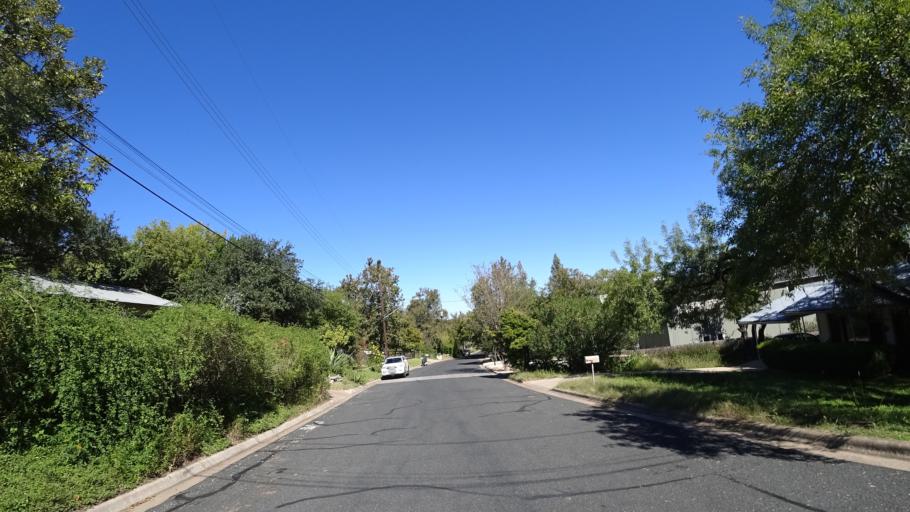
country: US
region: Texas
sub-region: Travis County
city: Austin
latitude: 30.2377
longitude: -97.7654
